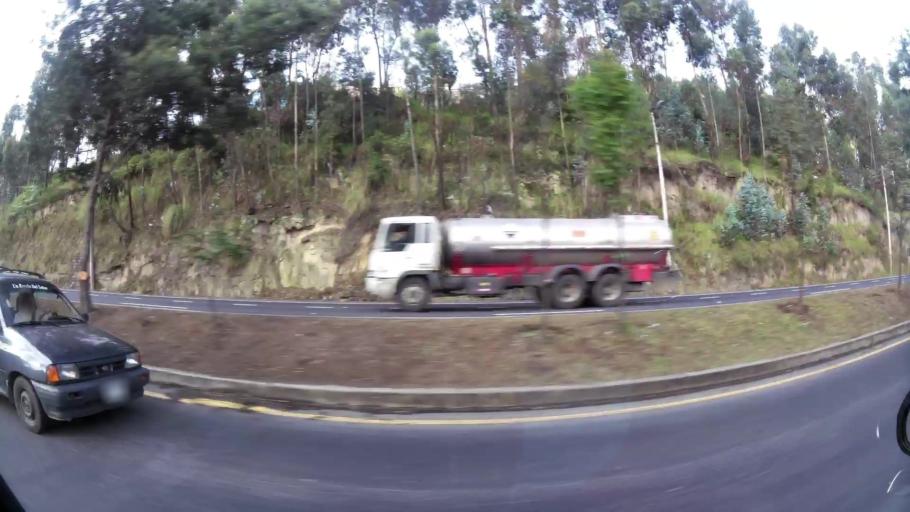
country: EC
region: Pichincha
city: Quito
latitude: -0.2419
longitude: -78.4829
